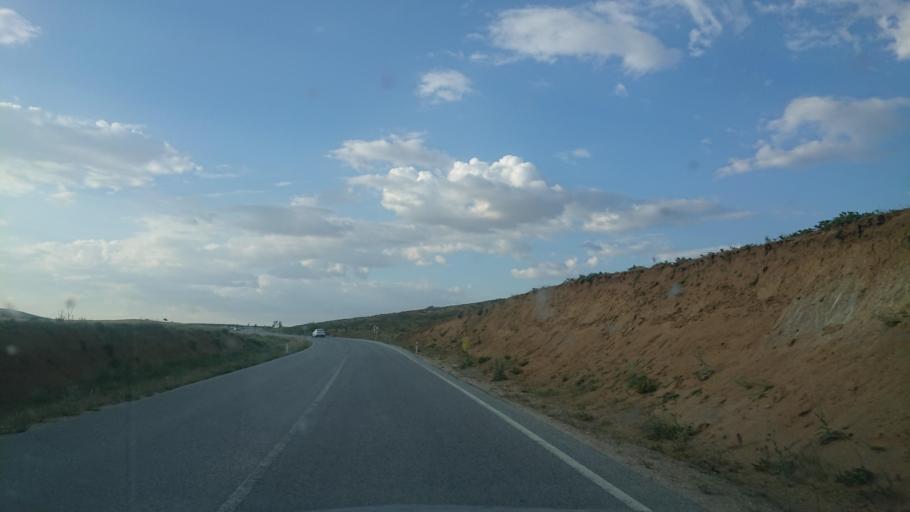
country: TR
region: Aksaray
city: Balci
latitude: 38.6081
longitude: 34.1020
